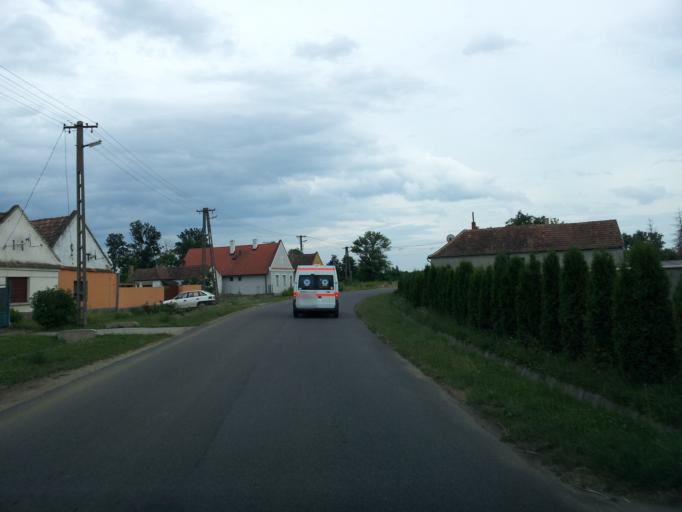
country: HU
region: Veszprem
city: Devecser
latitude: 47.1177
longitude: 17.3844
